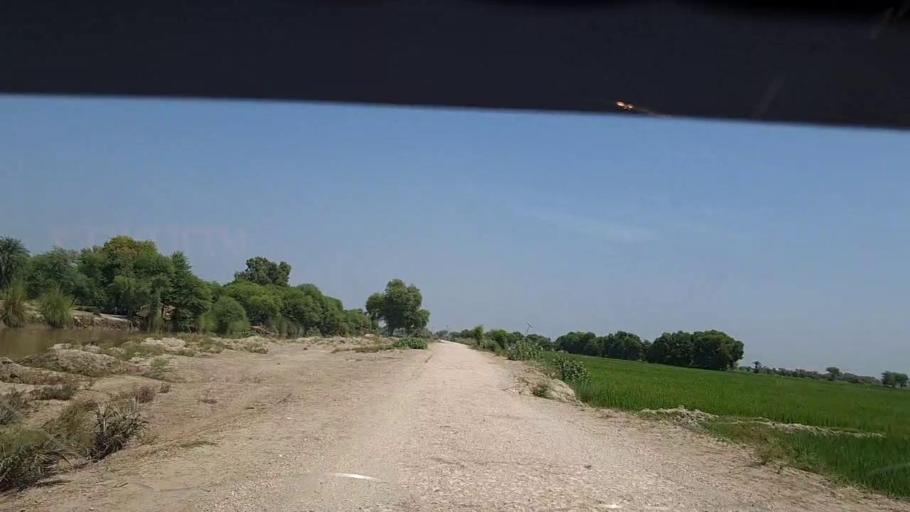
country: PK
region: Sindh
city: Tangwani
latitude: 28.2343
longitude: 68.9828
